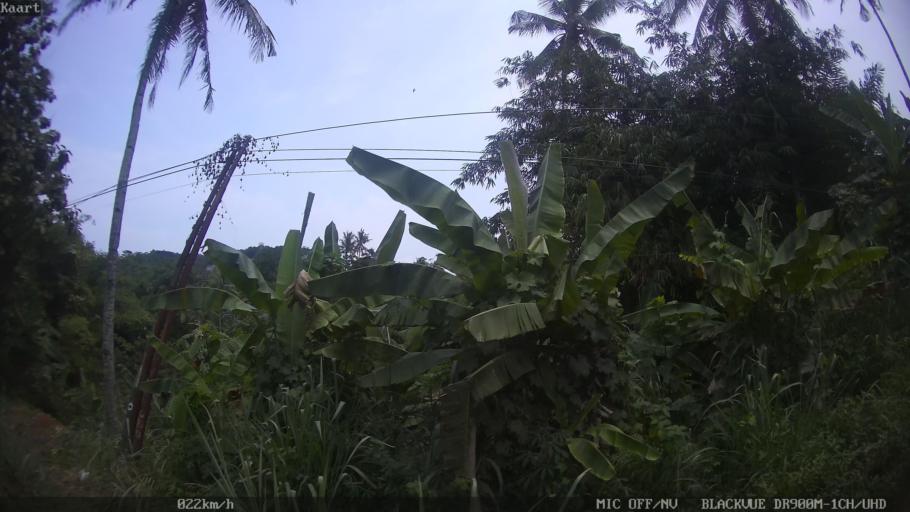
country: ID
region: Lampung
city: Bandarlampung
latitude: -5.4207
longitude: 105.2861
